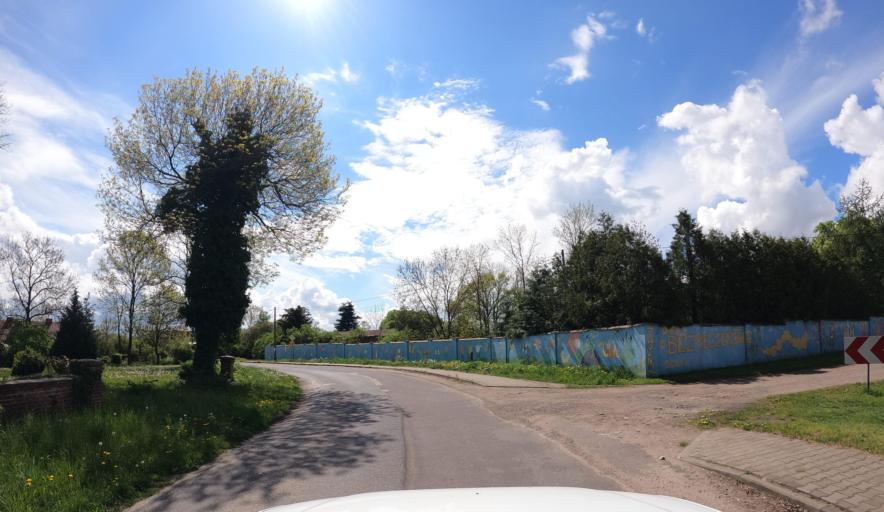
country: PL
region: West Pomeranian Voivodeship
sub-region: Powiat kamienski
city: Wolin
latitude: 53.9055
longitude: 14.6742
